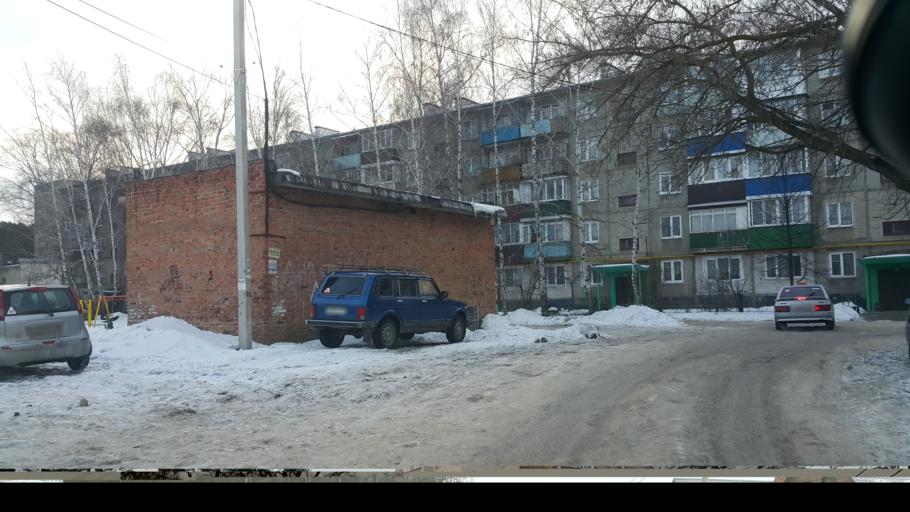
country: RU
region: Tambov
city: Kotovsk
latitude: 52.6020
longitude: 41.4935
